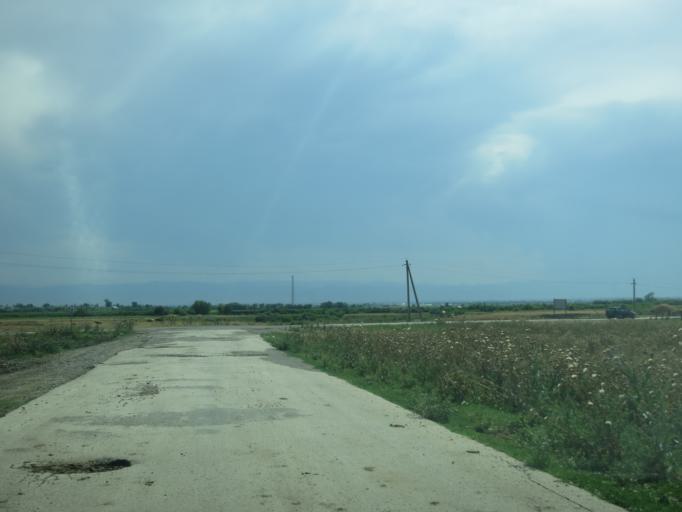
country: GE
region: Kvemo Kartli
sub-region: Gardabani
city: Gardabani
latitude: 41.4731
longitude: 45.1701
